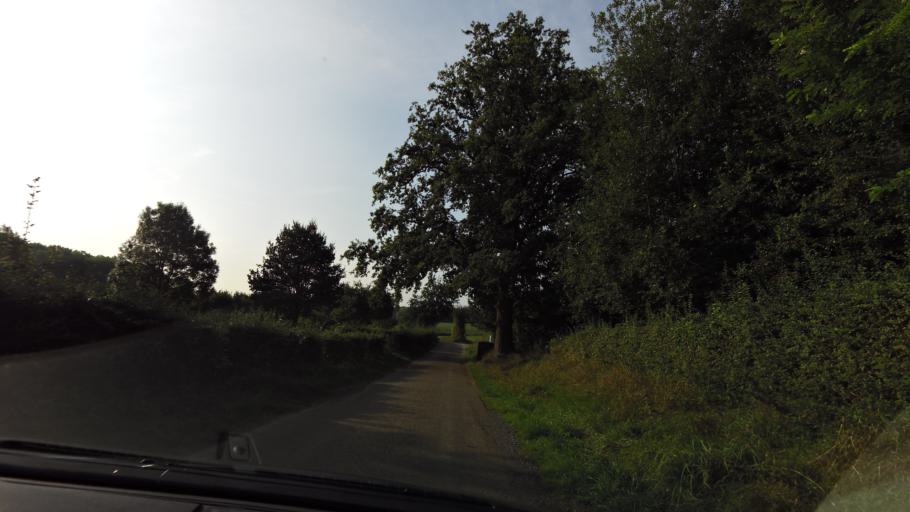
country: BE
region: Wallonia
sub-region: Province de Liege
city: Plombieres
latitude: 50.7657
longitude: 5.9225
